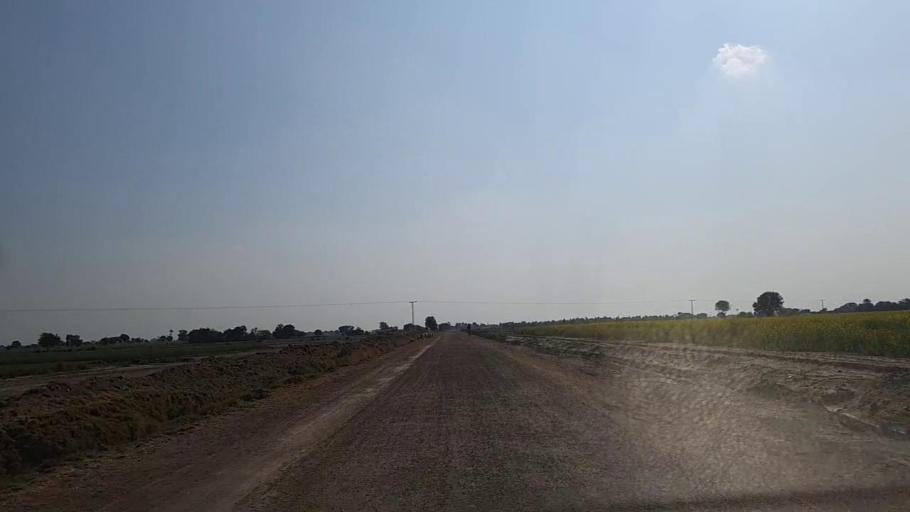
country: PK
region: Sindh
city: Jam Sahib
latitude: 26.2532
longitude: 68.5669
